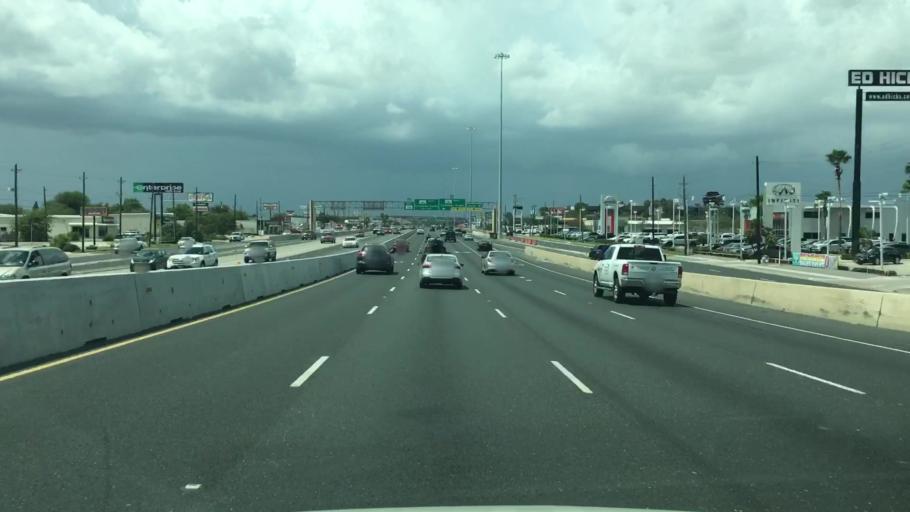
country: US
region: Texas
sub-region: Nueces County
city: Corpus Christi
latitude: 27.7296
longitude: -97.4149
